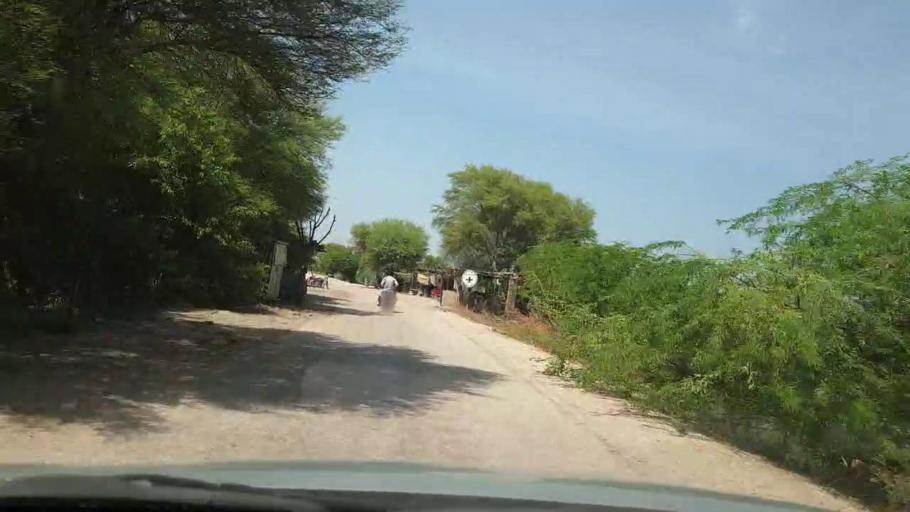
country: PK
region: Sindh
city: Pano Aqil
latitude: 27.7059
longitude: 69.1130
